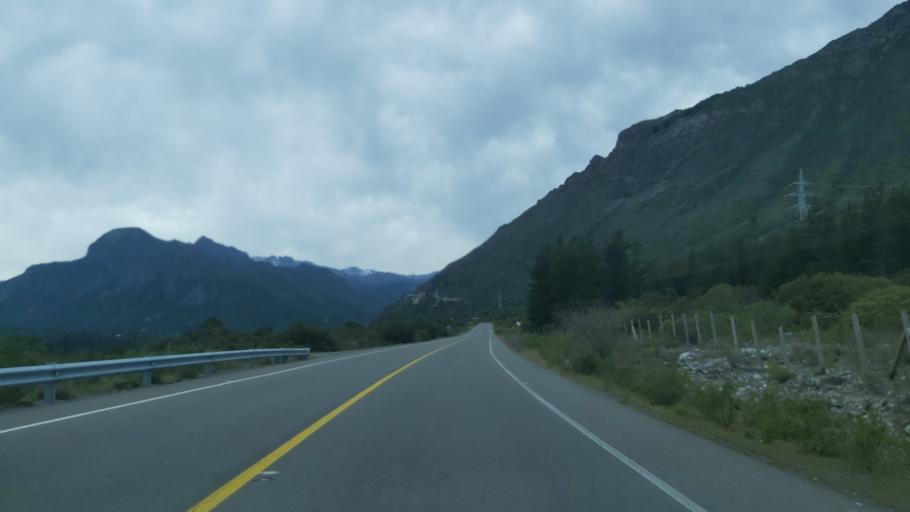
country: CL
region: Maule
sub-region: Provincia de Linares
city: Colbun
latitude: -35.7074
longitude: -71.0997
